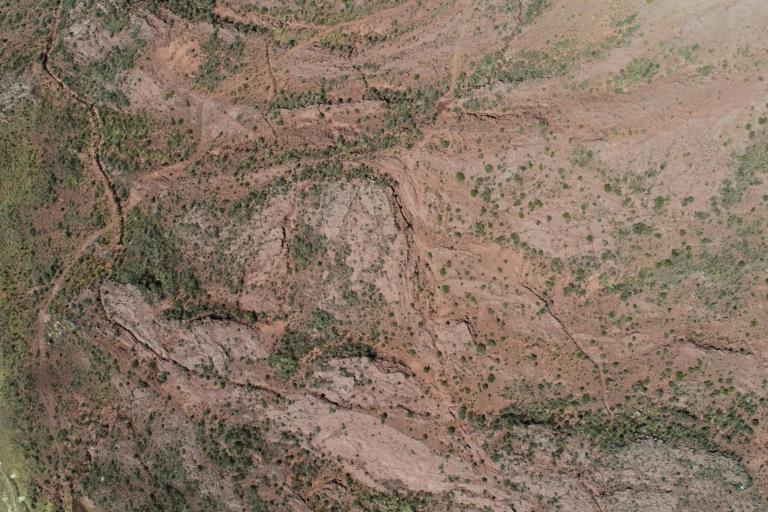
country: BO
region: La Paz
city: Tiahuanaco
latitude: -16.5973
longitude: -68.7565
